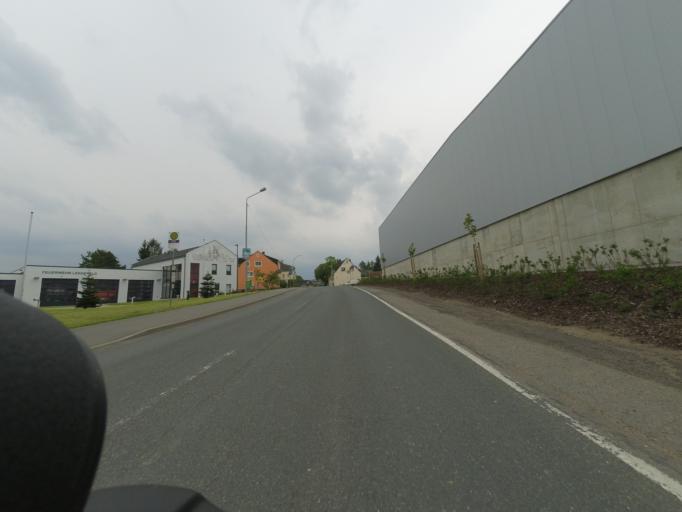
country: DE
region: Saxony
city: Lengefeld
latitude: 50.7222
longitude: 13.1910
